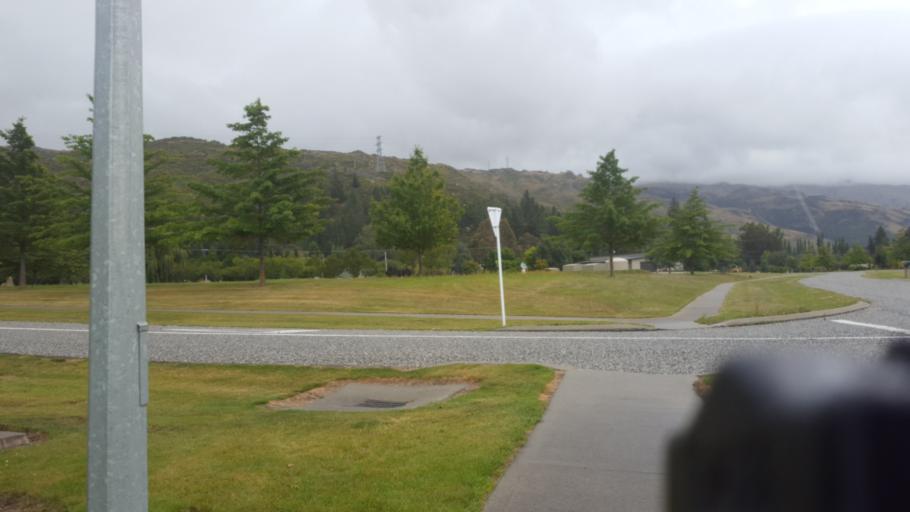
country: NZ
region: Otago
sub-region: Queenstown-Lakes District
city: Wanaka
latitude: -45.1965
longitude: 169.3171
